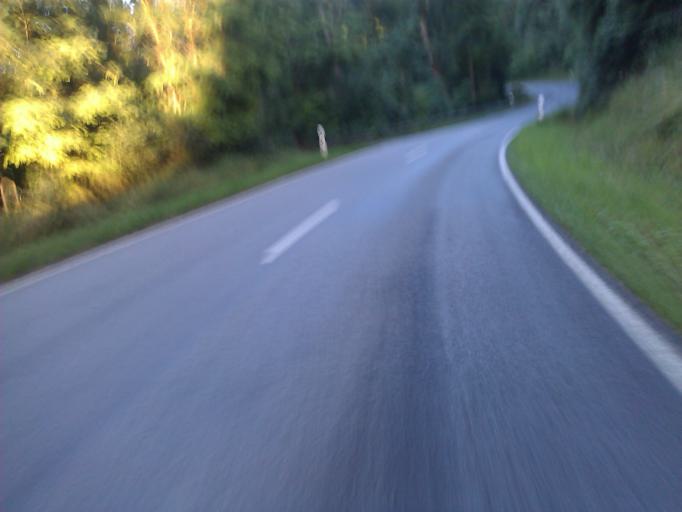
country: DE
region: Baden-Wuerttemberg
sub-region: Regierungsbezirk Stuttgart
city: Talheim
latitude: 49.0660
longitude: 9.2029
